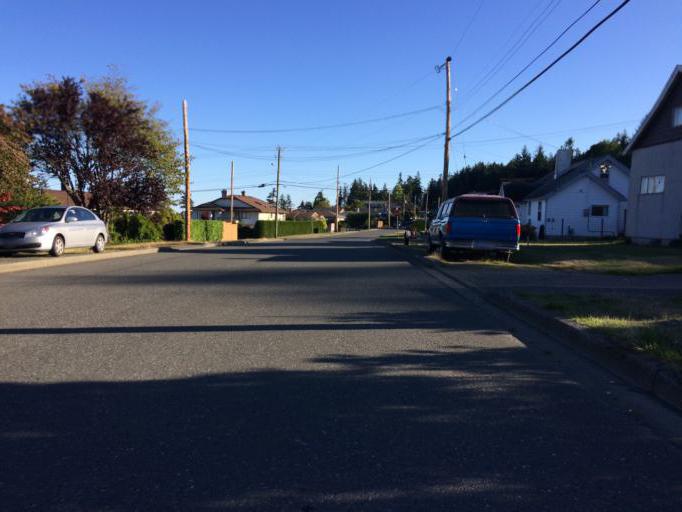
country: CA
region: British Columbia
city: Campbell River
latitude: 50.0200
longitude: -125.2393
